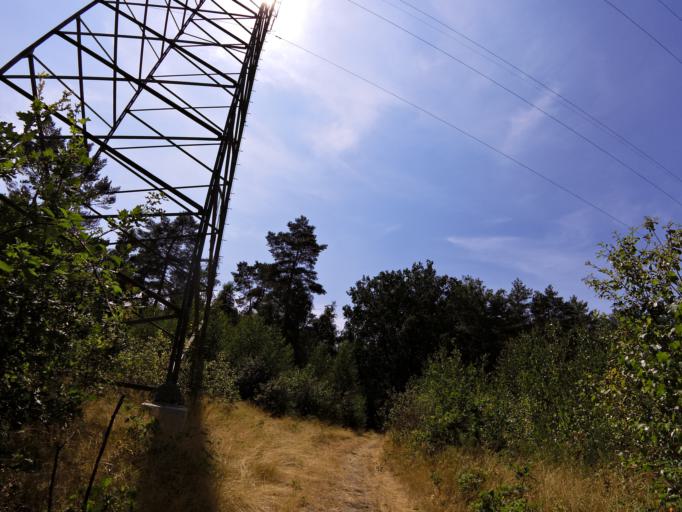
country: NL
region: Limburg
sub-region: Gemeente Leudal
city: Heythuysen
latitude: 51.2090
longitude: 5.8967
